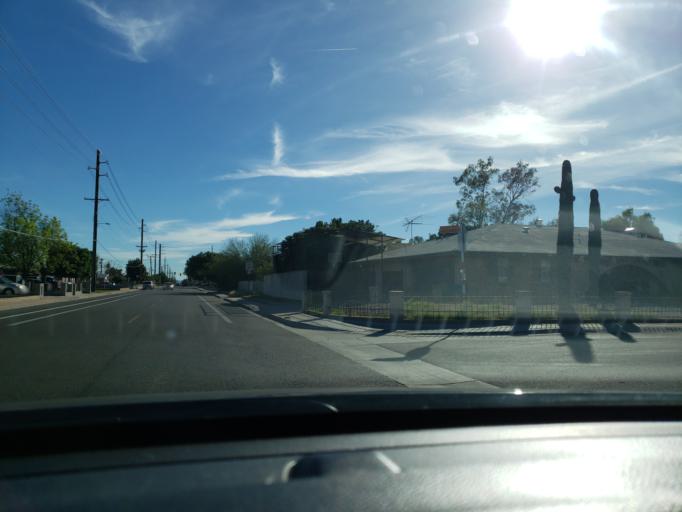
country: US
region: Arizona
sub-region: Maricopa County
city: Glendale
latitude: 33.5700
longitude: -112.1430
